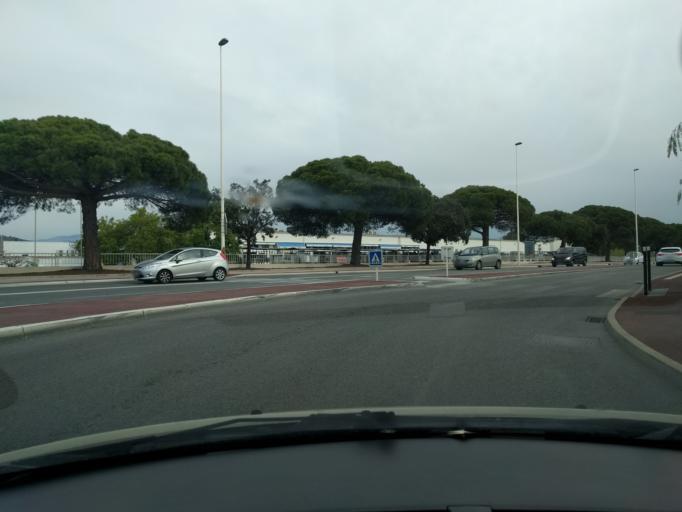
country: FR
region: Provence-Alpes-Cote d'Azur
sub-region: Departement des Alpes-Maritimes
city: Mandelieu-la-Napoule
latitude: 43.5435
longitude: 6.9601
